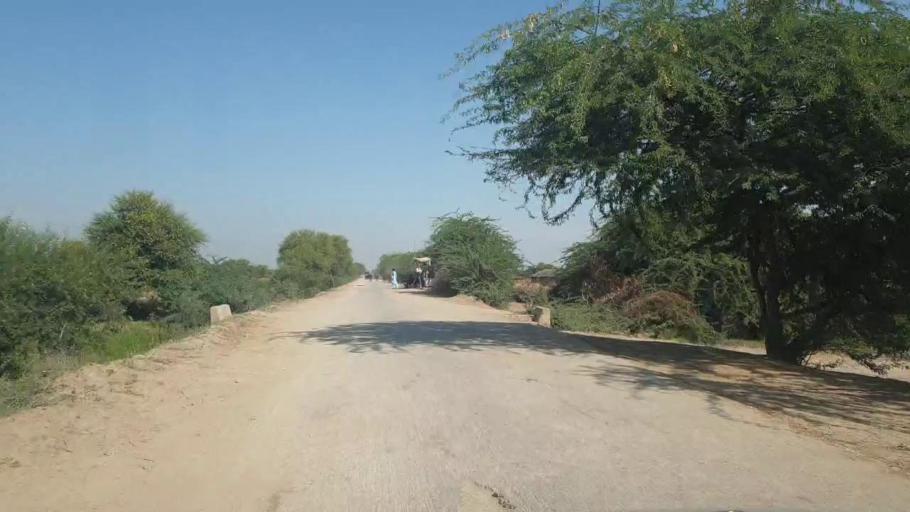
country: PK
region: Sindh
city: Tando Bago
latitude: 24.8006
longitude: 68.9773
